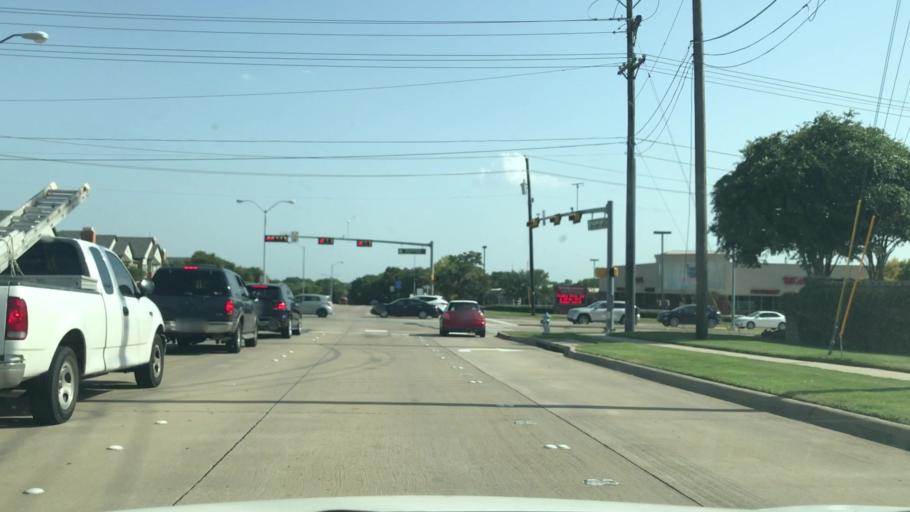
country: US
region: Texas
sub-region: Collin County
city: Allen
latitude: 33.1013
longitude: -96.7503
